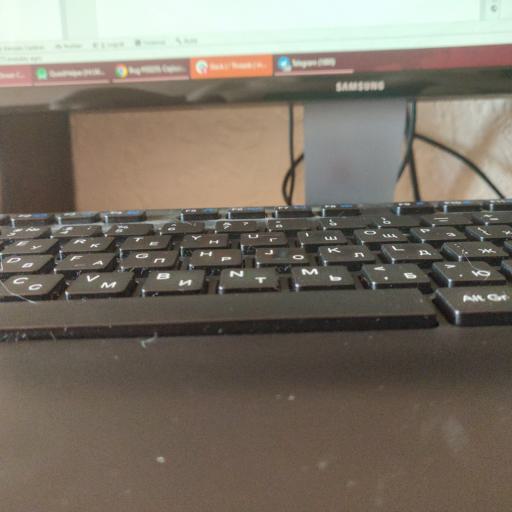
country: FI
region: Haeme
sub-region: Forssa
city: Jokioinen
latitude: 60.7823
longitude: 23.4757
